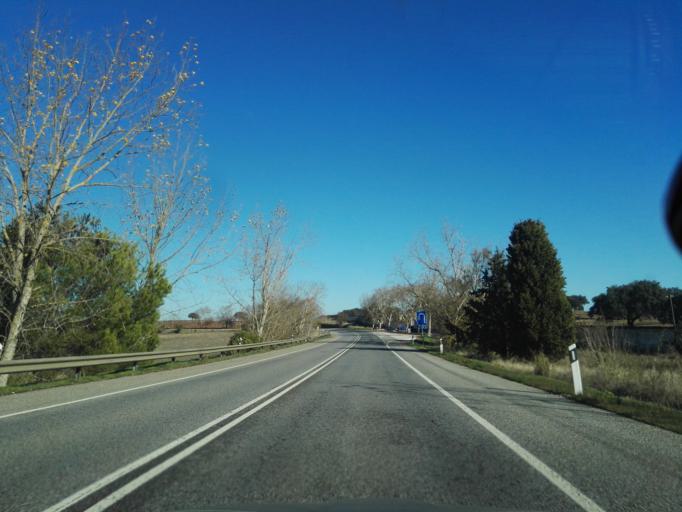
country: PT
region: Evora
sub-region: Borba
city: Borba
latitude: 38.8264
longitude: -7.4129
